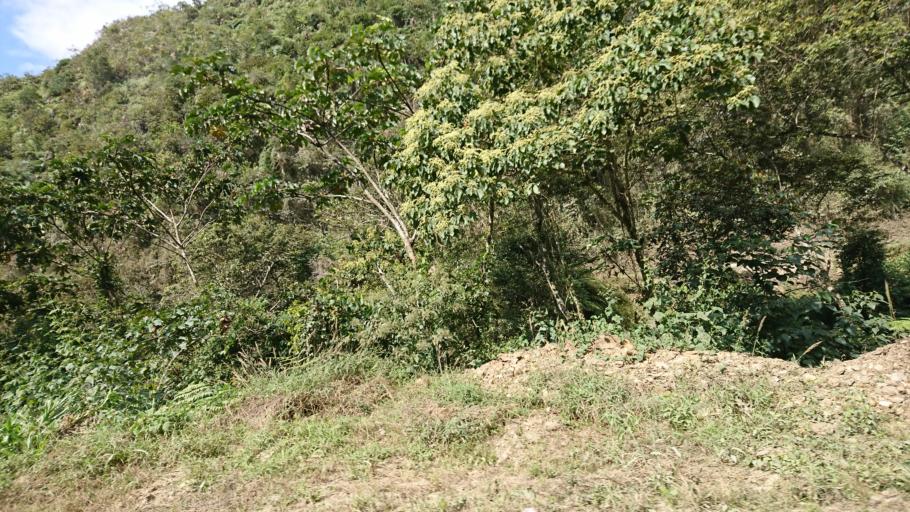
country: BO
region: La Paz
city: Coroico
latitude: -16.1282
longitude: -67.7653
